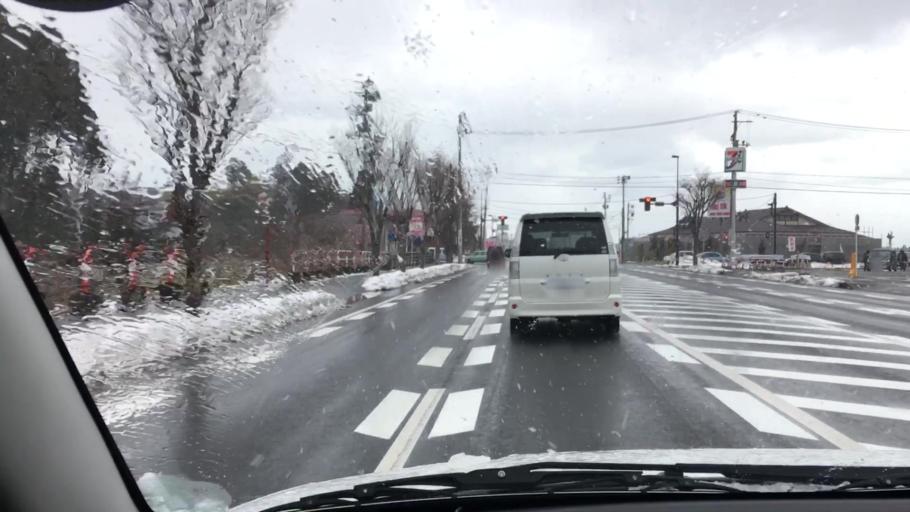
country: JP
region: Niigata
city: Joetsu
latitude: 37.1228
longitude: 138.2323
